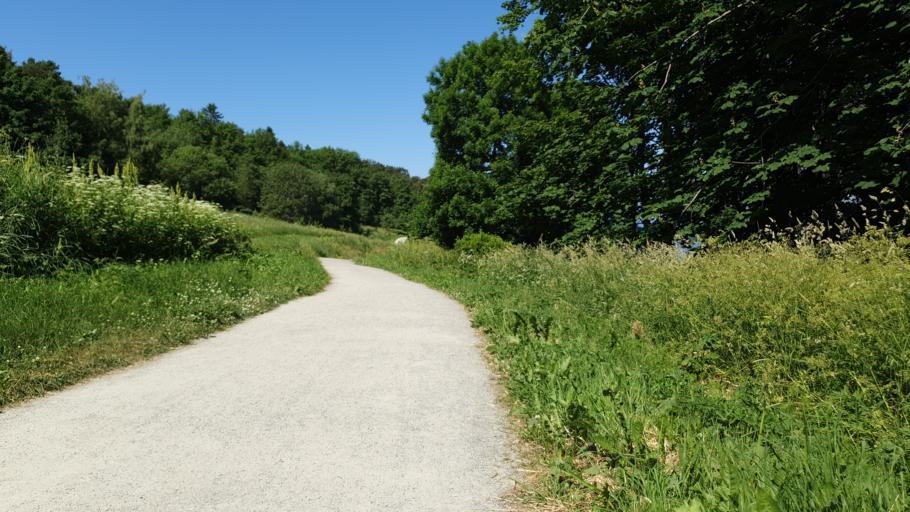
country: NO
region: Sor-Trondelag
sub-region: Trondheim
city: Trondheim
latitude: 63.4403
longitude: 10.4708
